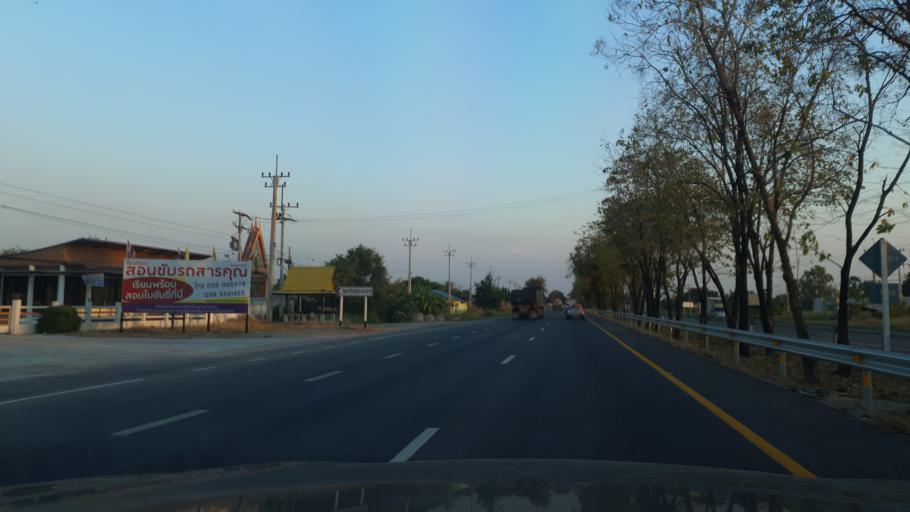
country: TH
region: Nakhon Sawan
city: Banphot Phisai
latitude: 15.8077
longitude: 99.9505
